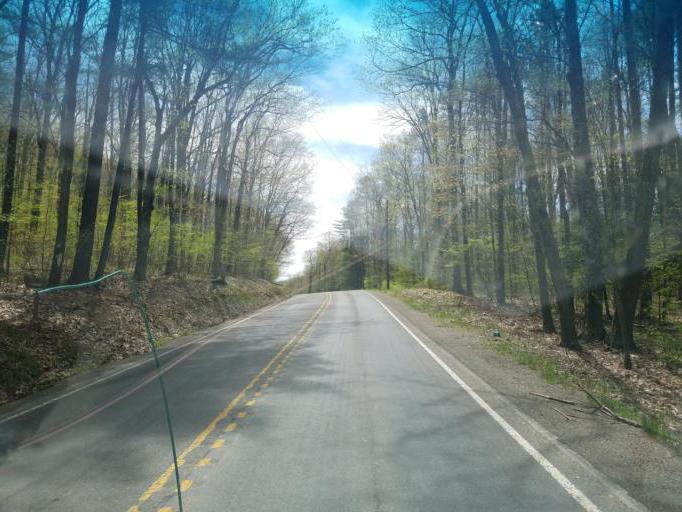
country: US
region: Pennsylvania
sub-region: Tioga County
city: Wellsboro
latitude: 41.7314
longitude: -77.4259
